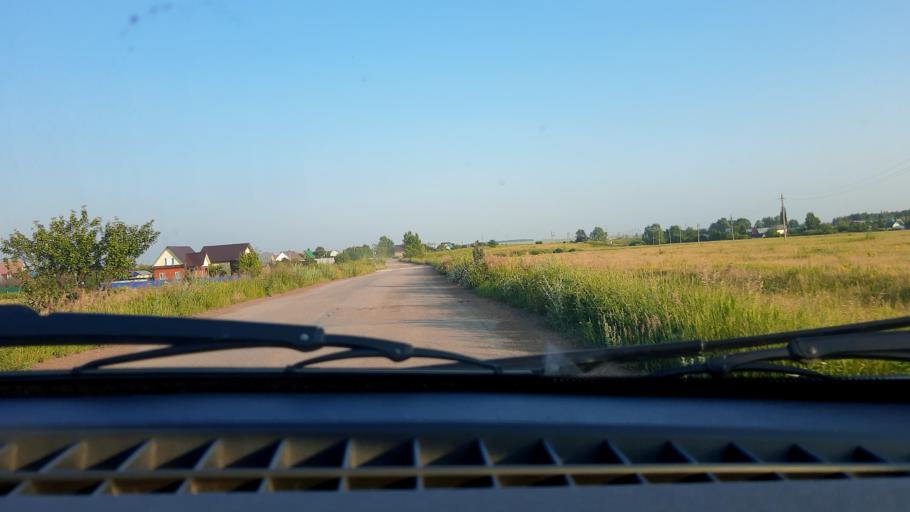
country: RU
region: Bashkortostan
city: Asanovo
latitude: 54.9186
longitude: 55.6256
